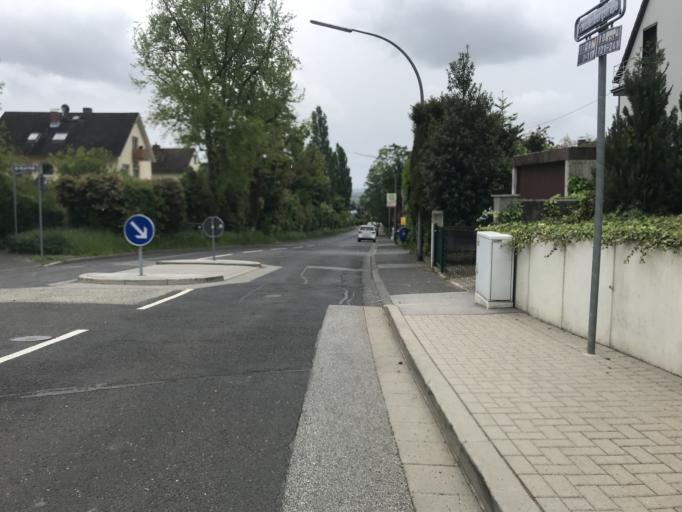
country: DE
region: Hesse
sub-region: Regierungsbezirk Darmstadt
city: Walluf
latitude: 50.0581
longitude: 8.1914
